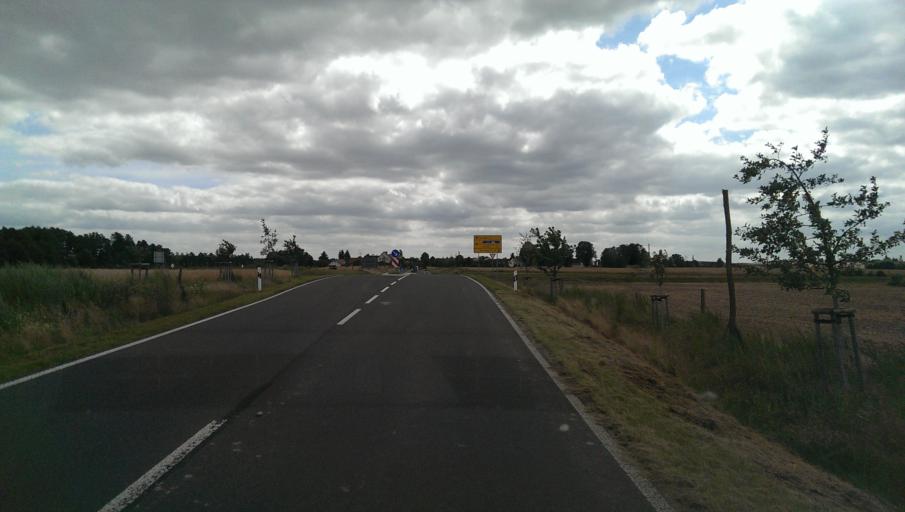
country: DE
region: Brandenburg
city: Niemegk
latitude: 52.1074
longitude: 12.6748
